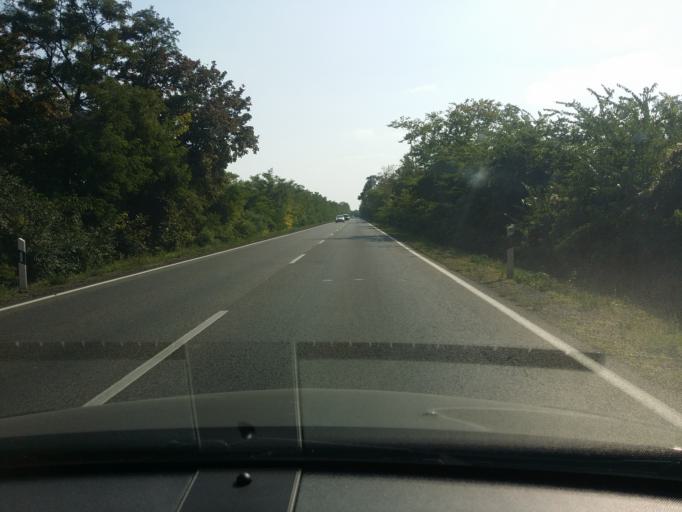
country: HU
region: Fejer
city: dunaujvaros
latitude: 46.9534
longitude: 18.9118
